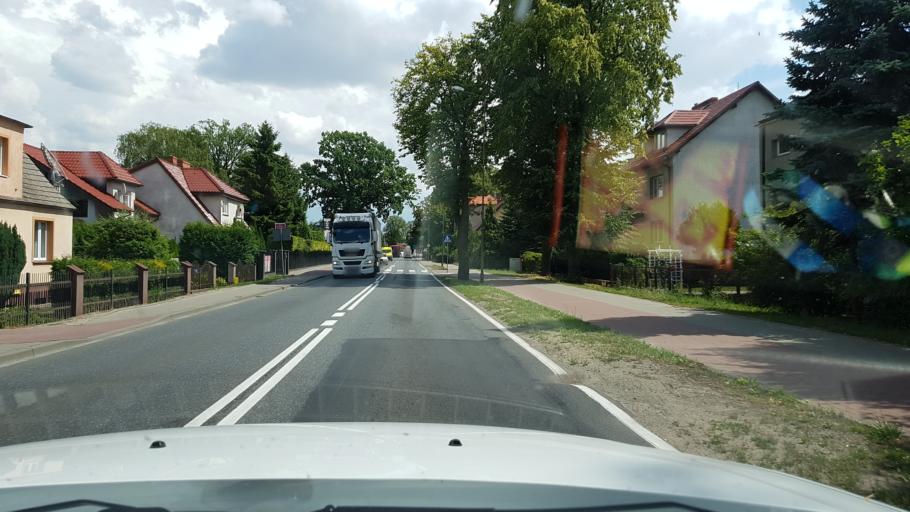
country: PL
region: West Pomeranian Voivodeship
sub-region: Powiat walecki
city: Walcz
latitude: 53.2792
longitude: 16.4584
